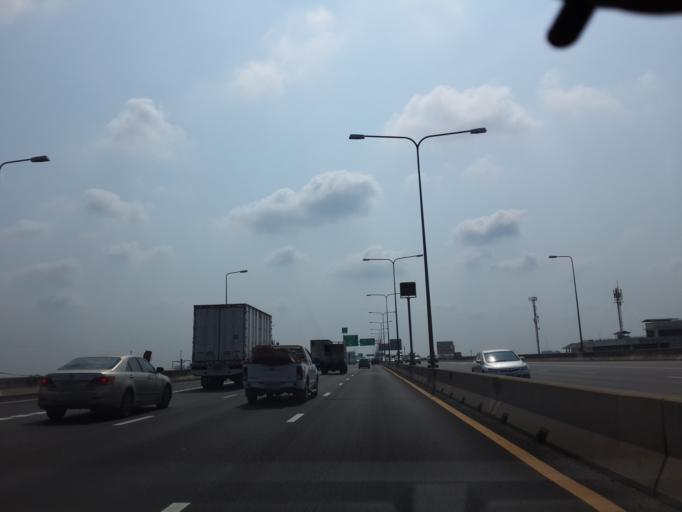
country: TH
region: Bangkok
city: Bang Na
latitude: 13.6443
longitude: 100.6921
